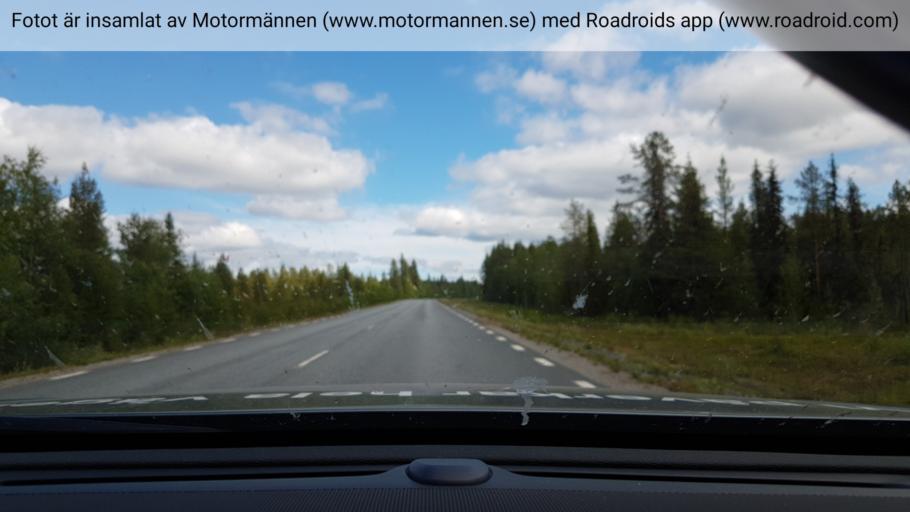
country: SE
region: Vaesterbotten
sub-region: Sorsele Kommun
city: Sorsele
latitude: 65.5371
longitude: 17.5888
